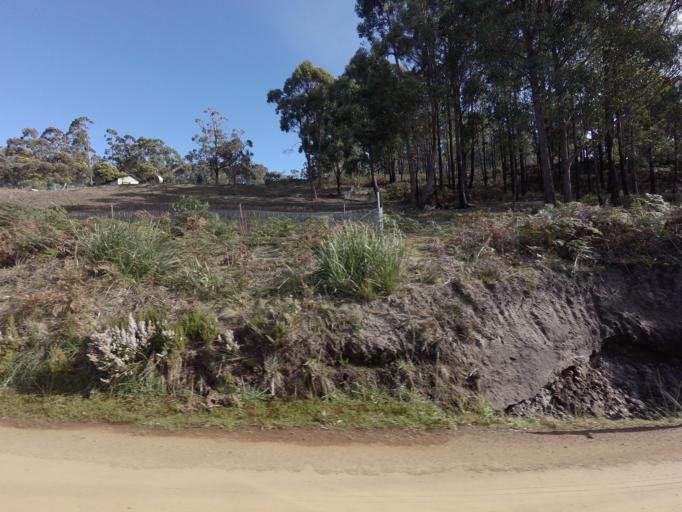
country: AU
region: Tasmania
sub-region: Kingborough
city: Kettering
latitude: -43.0854
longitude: 147.2637
